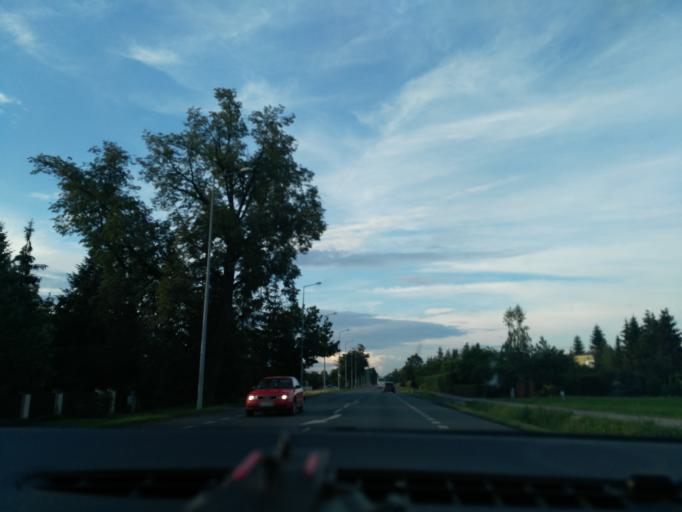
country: PL
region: Lublin Voivodeship
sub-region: Powiat lubelski
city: Niedrzwica Duza
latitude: 51.0960
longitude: 22.3683
